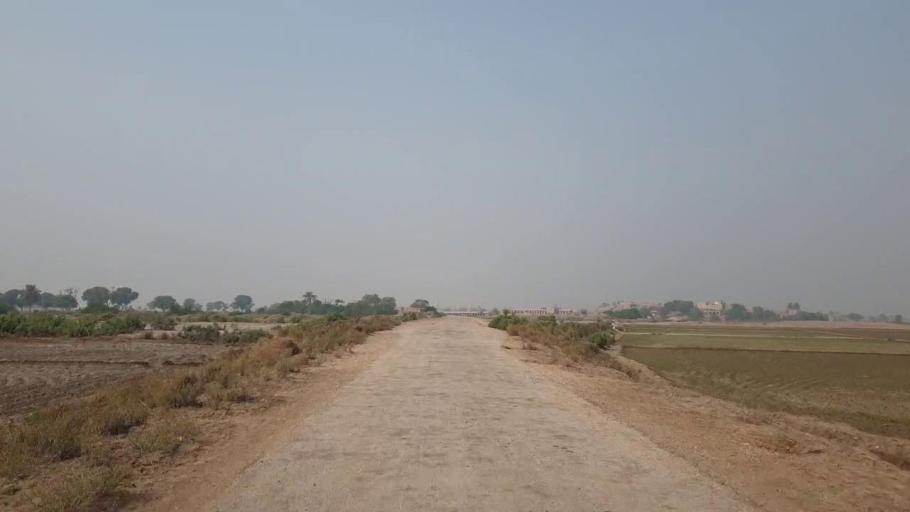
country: PK
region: Sindh
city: Bhan
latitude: 26.5023
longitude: 67.6934
